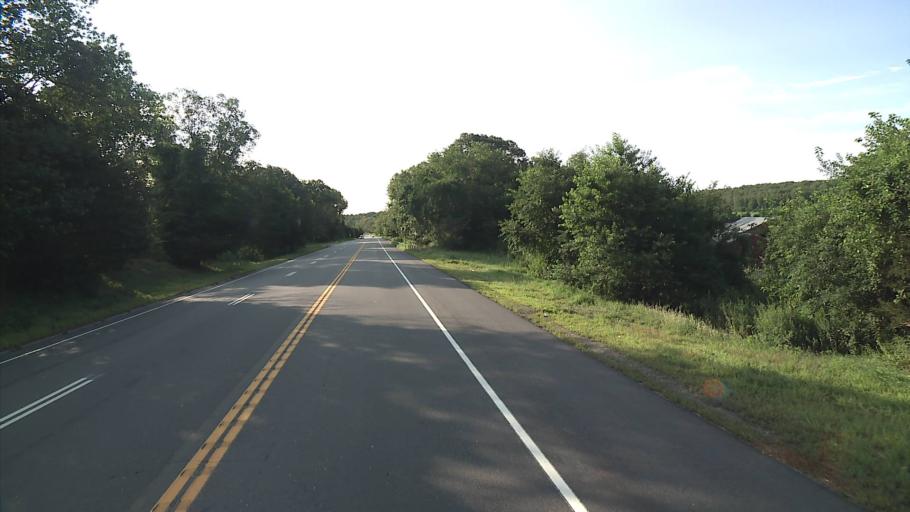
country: US
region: Connecticut
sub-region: New London County
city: Norwich
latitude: 41.5060
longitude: -72.0426
